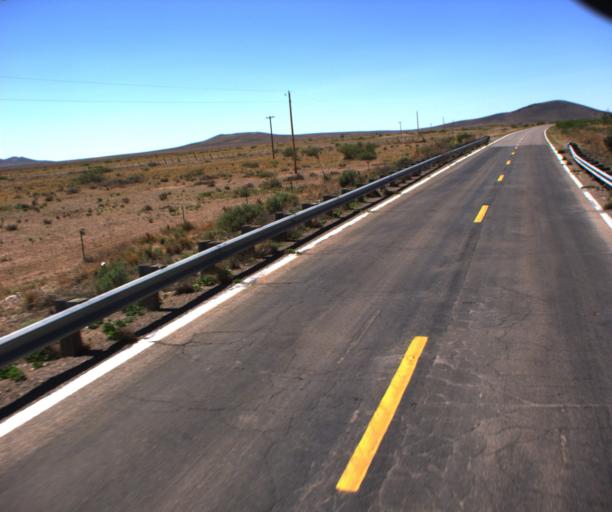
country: US
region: Arizona
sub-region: Cochise County
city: Douglas
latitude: 31.6509
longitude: -109.1617
